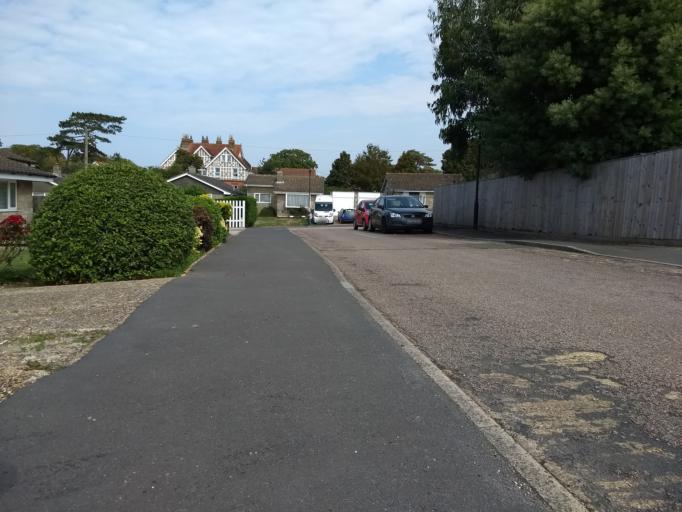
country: GB
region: England
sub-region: Isle of Wight
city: Newport
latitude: 50.7060
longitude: -1.2822
